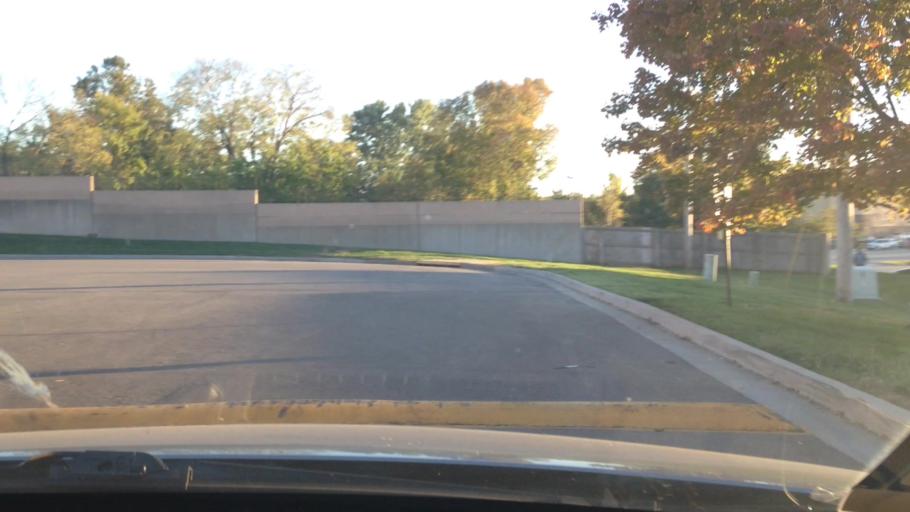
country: US
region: Kansas
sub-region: Johnson County
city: Lenexa
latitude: 38.9098
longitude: -94.7656
